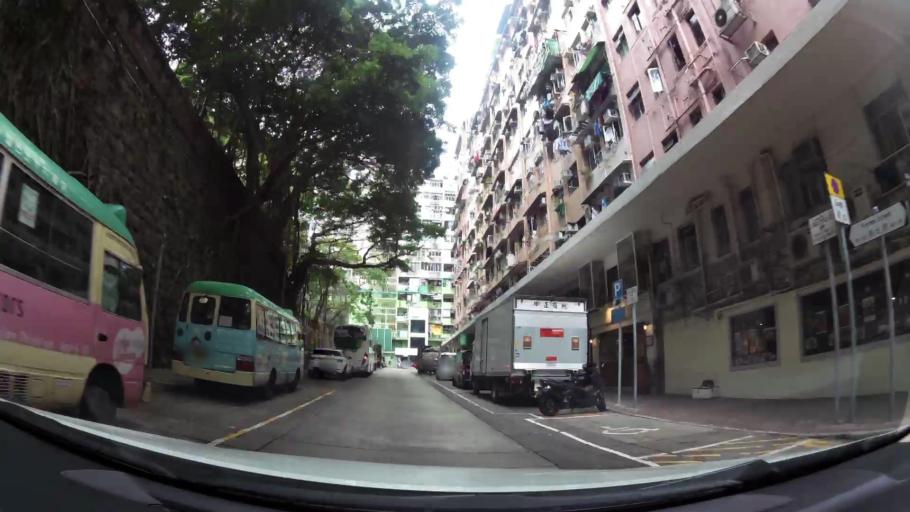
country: HK
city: Hong Kong
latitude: 22.2812
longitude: 114.1270
